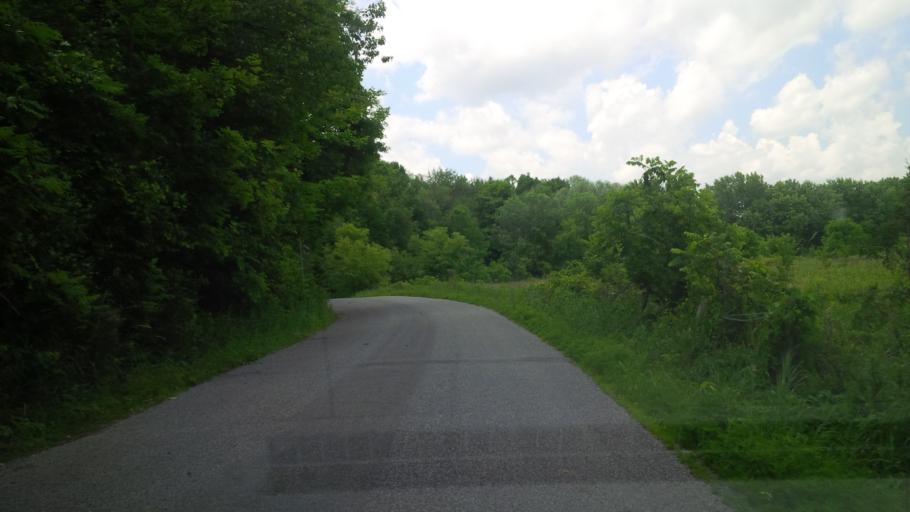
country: CA
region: Ontario
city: Burlington
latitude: 43.4325
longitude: -79.8633
